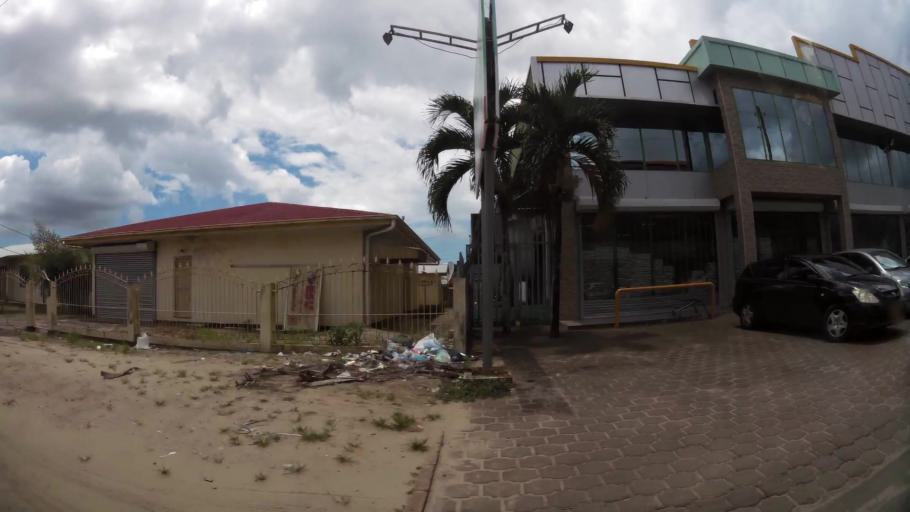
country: SR
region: Paramaribo
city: Paramaribo
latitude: 5.8546
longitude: -55.1379
